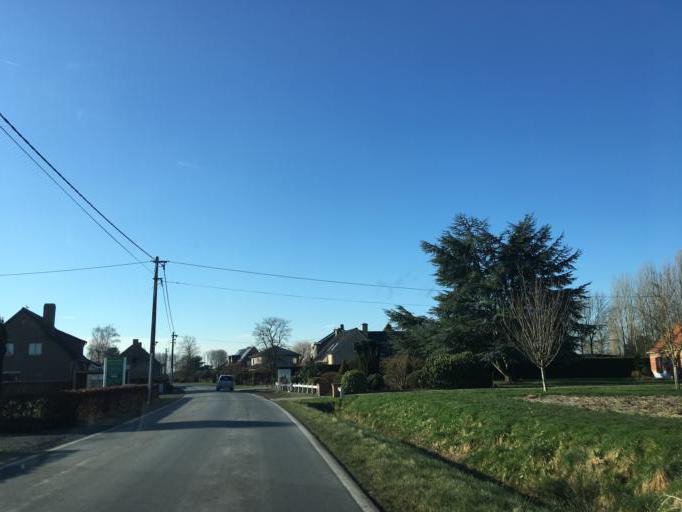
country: BE
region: Flanders
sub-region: Provincie Oost-Vlaanderen
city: Zomergem
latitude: 51.1217
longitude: 3.5879
